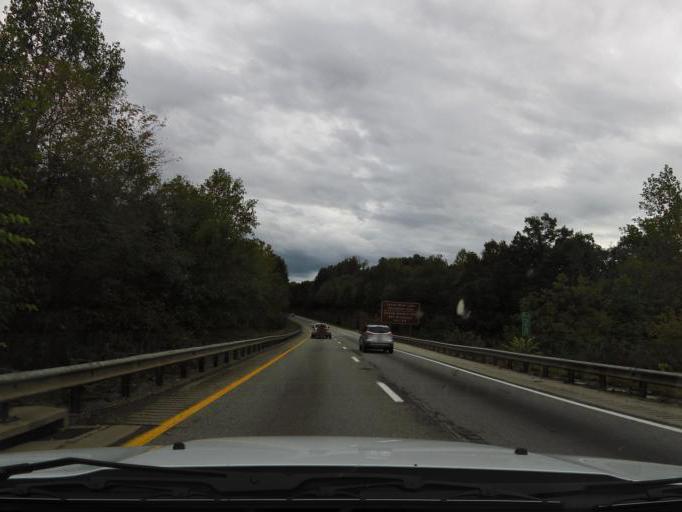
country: US
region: Kentucky
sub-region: Laurel County
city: North Corbin
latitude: 36.9644
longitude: -84.1140
